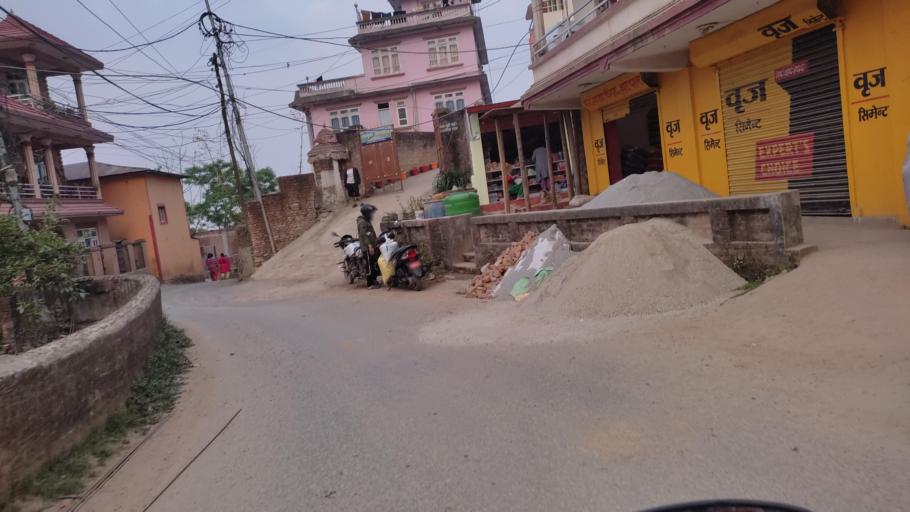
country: NP
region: Central Region
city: Kirtipur
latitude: 27.6670
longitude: 85.2495
